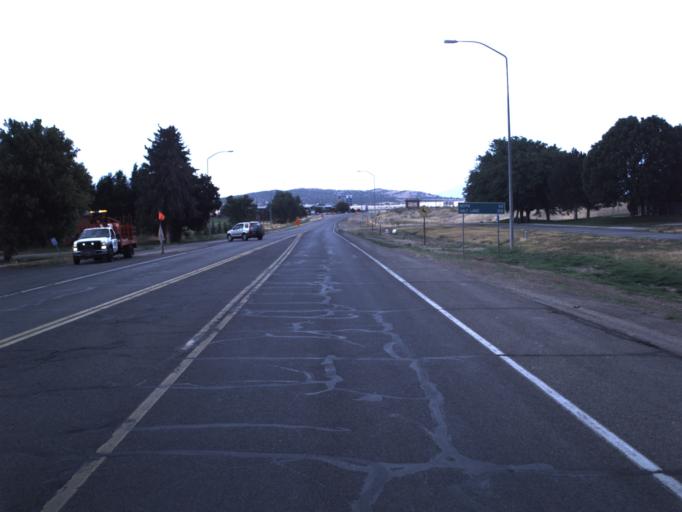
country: US
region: Utah
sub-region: Millard County
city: Fillmore
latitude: 38.9823
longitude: -112.3237
